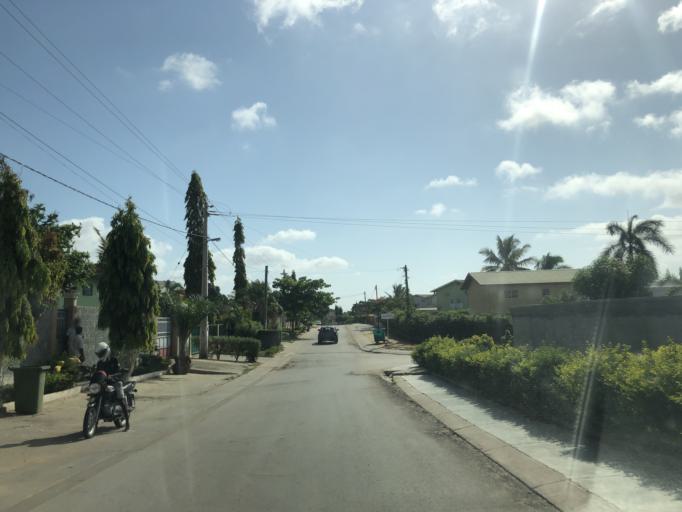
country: AO
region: Luanda
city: Luanda
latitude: -8.9074
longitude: 13.2283
